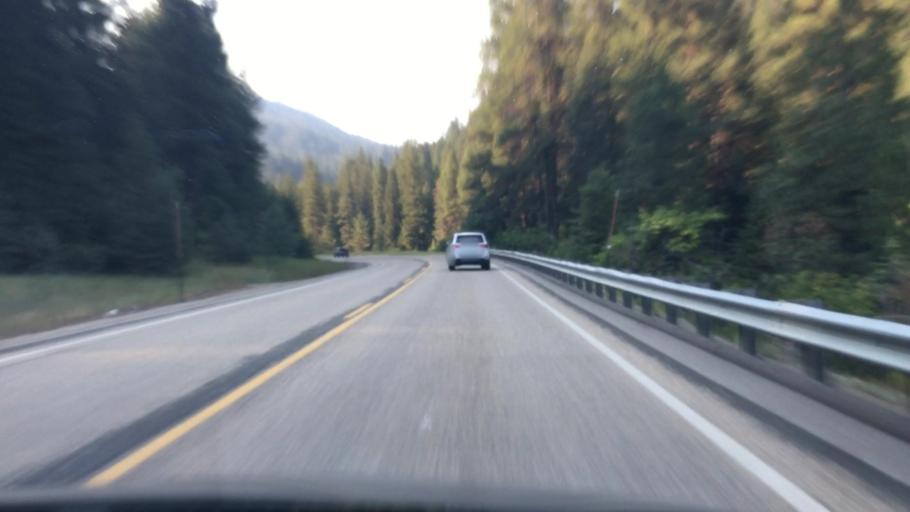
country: US
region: Idaho
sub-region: Valley County
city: Cascade
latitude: 44.1632
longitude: -116.1180
